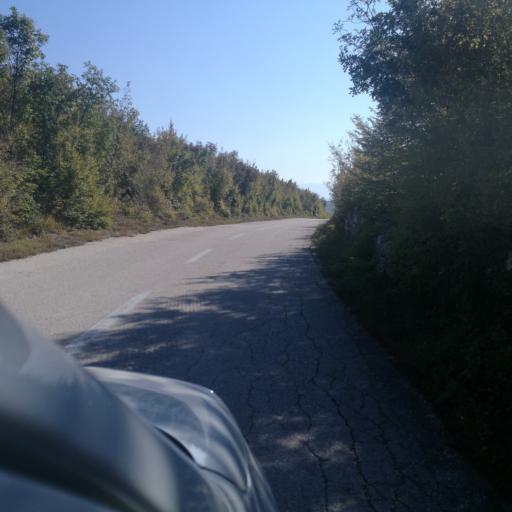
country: HR
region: Splitsko-Dalmatinska
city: Trilj
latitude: 43.5226
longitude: 16.7506
